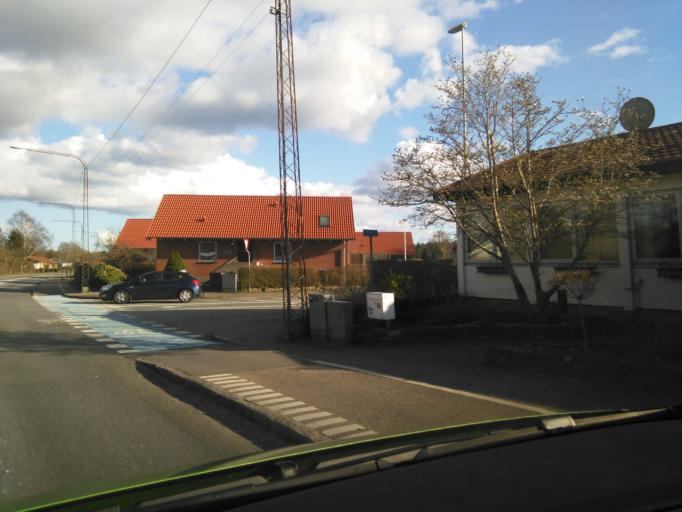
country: DK
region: Central Jutland
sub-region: Silkeborg Kommune
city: Silkeborg
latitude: 56.1763
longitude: 9.5234
